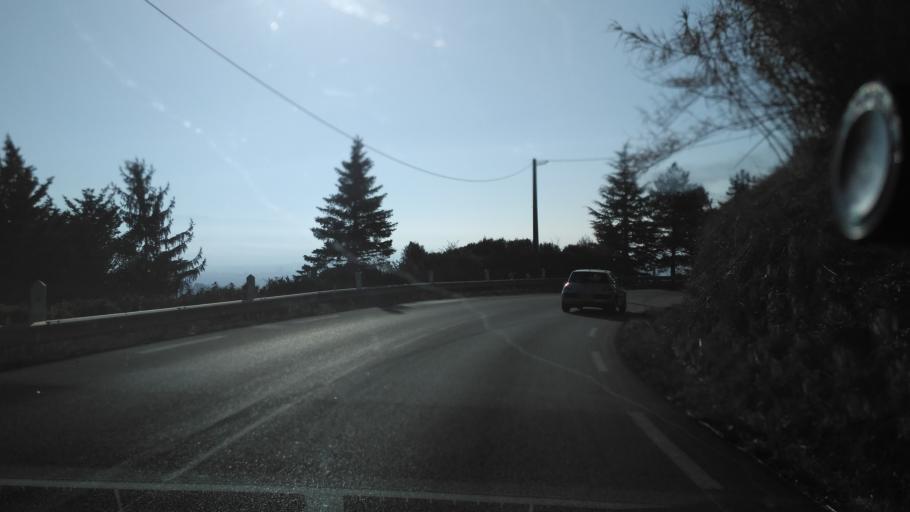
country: FR
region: Rhone-Alpes
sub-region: Departement de la Drome
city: Genissieux
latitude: 45.0957
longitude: 5.0906
